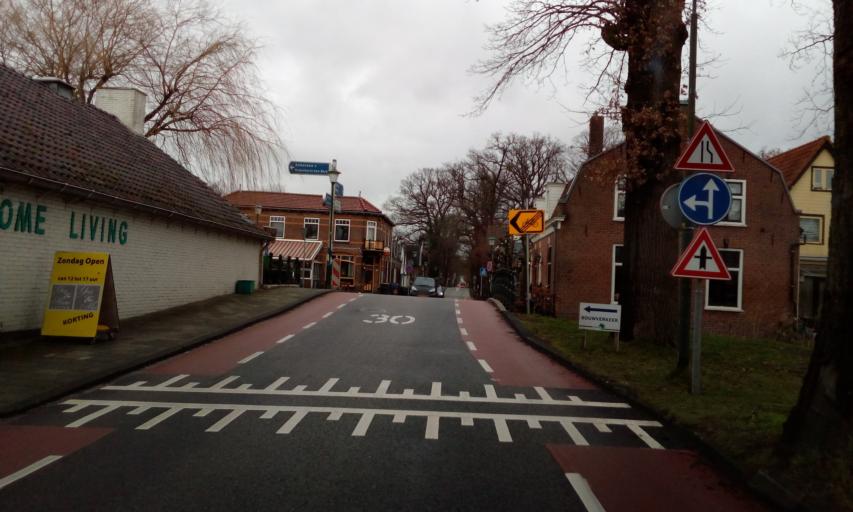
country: NL
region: North Holland
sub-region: Gemeente Wijdemeren
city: Kortenhoef
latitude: 52.2484
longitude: 5.1213
